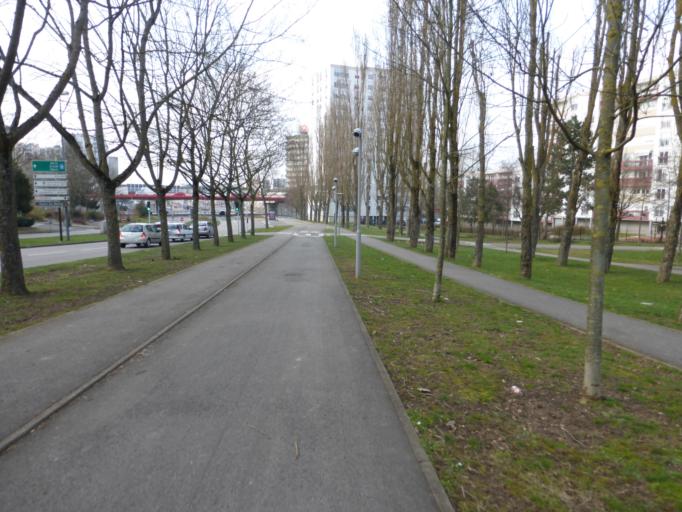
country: FR
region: Lorraine
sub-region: Departement de Meurthe-et-Moselle
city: Vandoeuvre-les-Nancy
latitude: 48.6597
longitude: 6.1770
